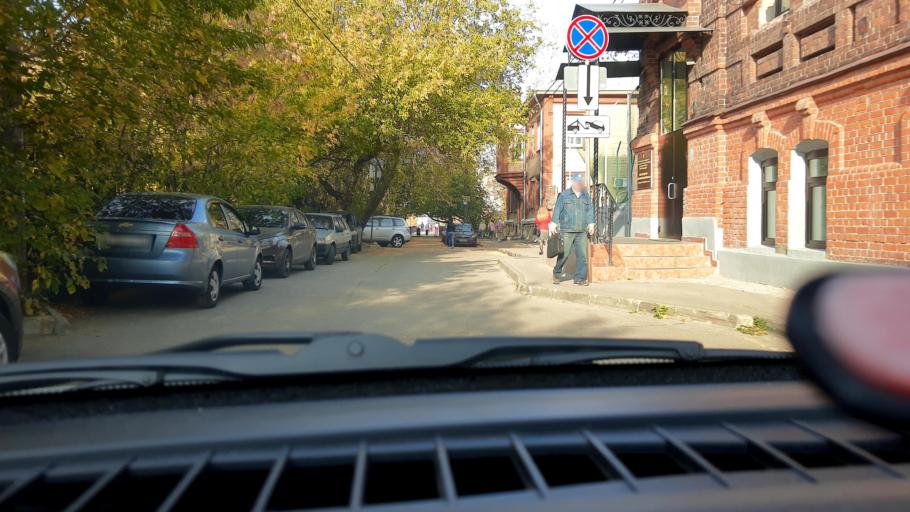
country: RU
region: Nizjnij Novgorod
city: Nizhniy Novgorod
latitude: 56.3197
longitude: 43.9938
